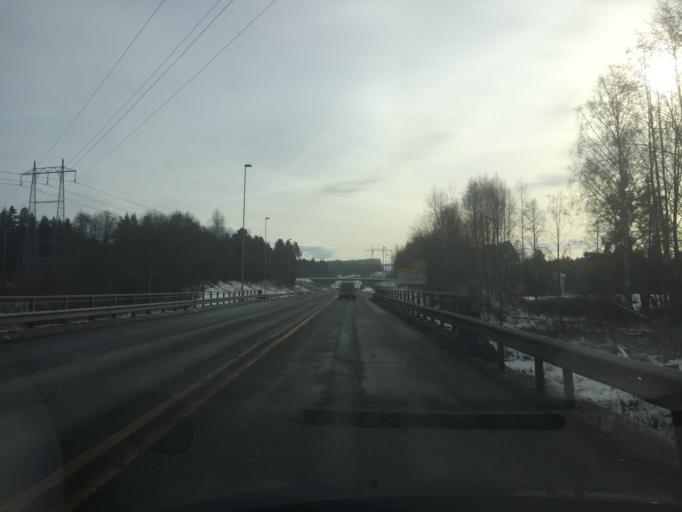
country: NO
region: Hedmark
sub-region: Loten
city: Loten
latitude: 60.7896
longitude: 11.2993
